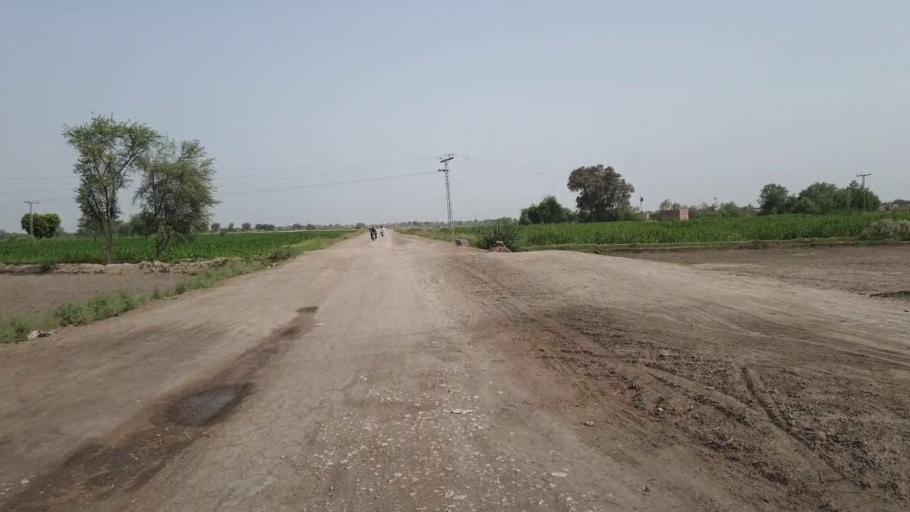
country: PK
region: Sindh
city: Daulatpur
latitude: 26.5545
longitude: 67.9904
